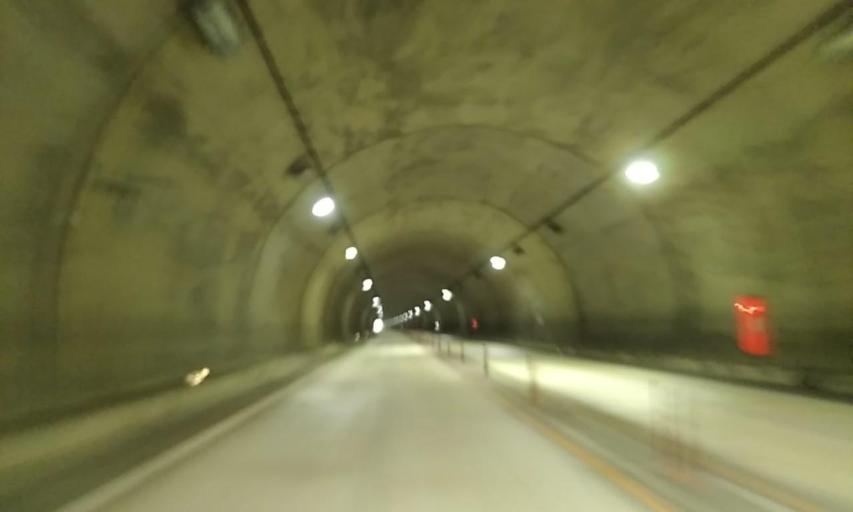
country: JP
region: Wakayama
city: Shingu
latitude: 33.6019
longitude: 135.9162
